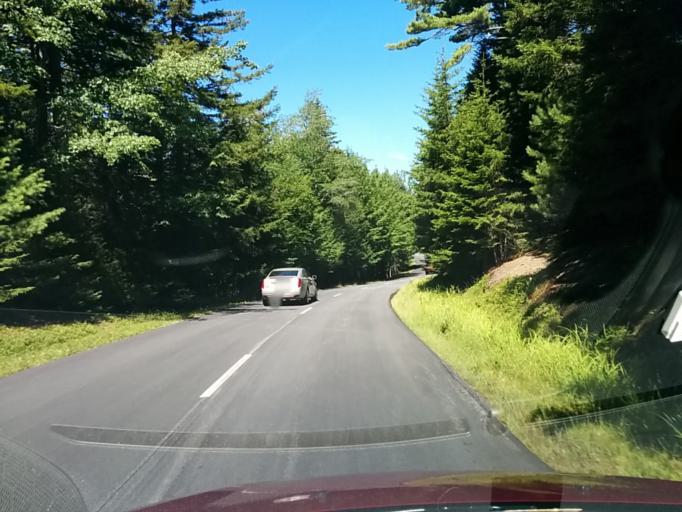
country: US
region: Maine
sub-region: Hancock County
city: Bar Harbor
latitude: 44.3068
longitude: -68.2204
